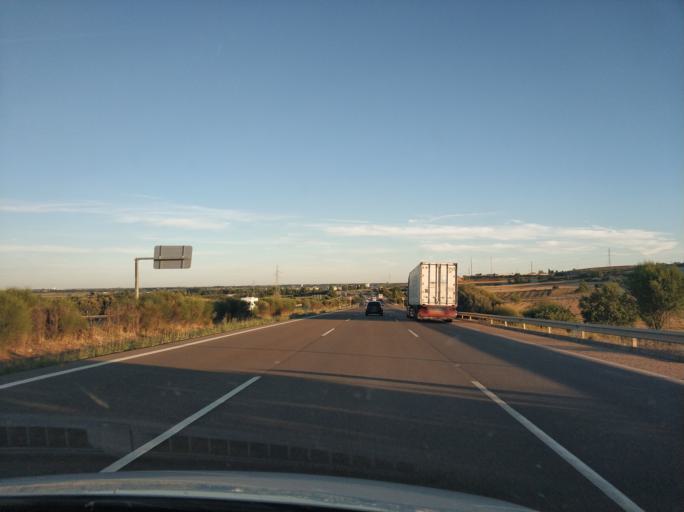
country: ES
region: Castille and Leon
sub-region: Provincia de Zamora
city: Benavente
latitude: 42.0291
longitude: -5.6712
